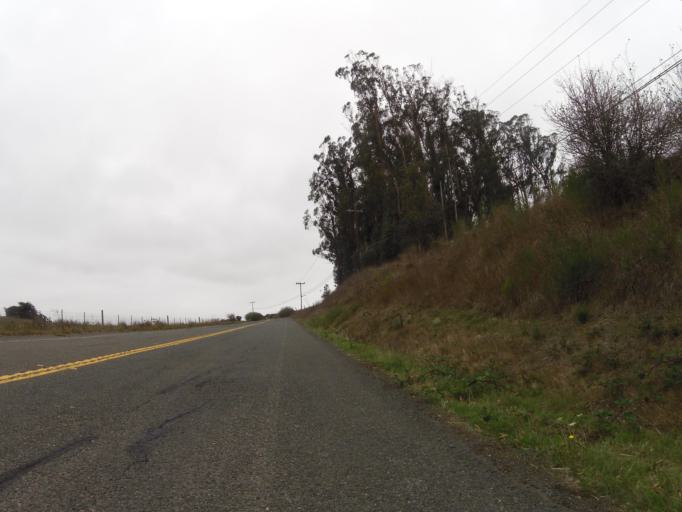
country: US
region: California
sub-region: Sonoma County
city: Occidental
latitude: 38.2601
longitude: -122.9020
